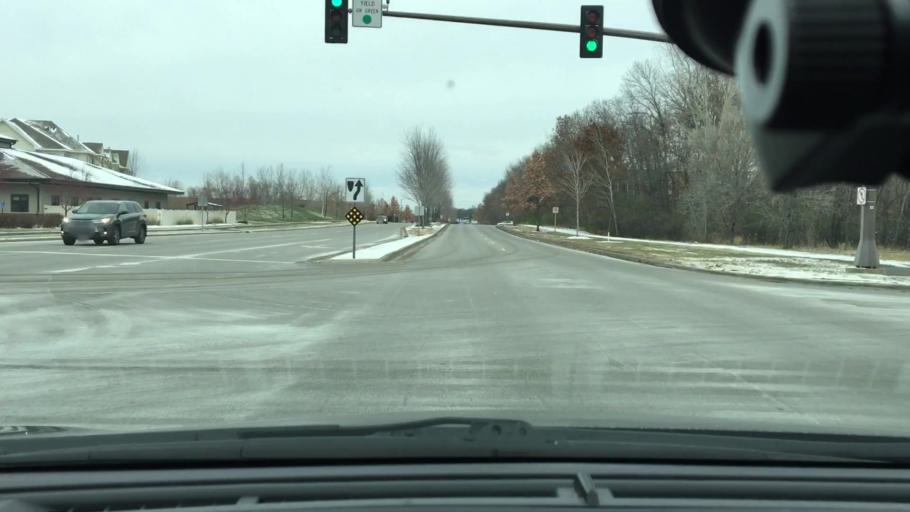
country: US
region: Minnesota
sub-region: Hennepin County
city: Maple Grove
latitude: 45.1193
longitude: -93.4924
